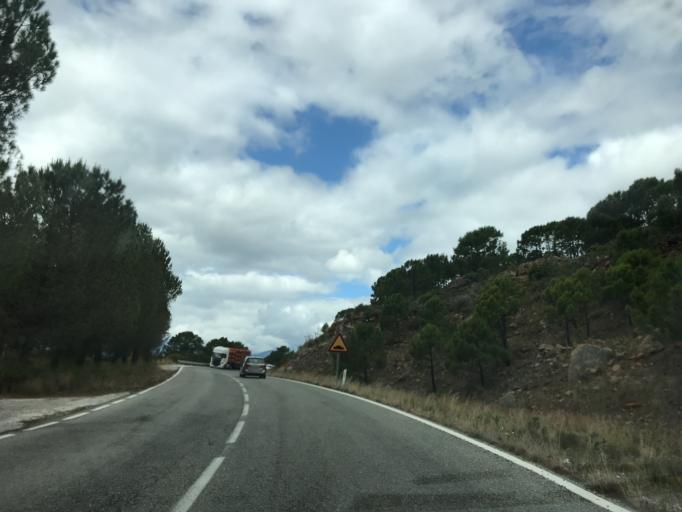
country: ES
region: Andalusia
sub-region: Provincia de Malaga
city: Benahavis
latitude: 36.5555
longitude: -5.0393
